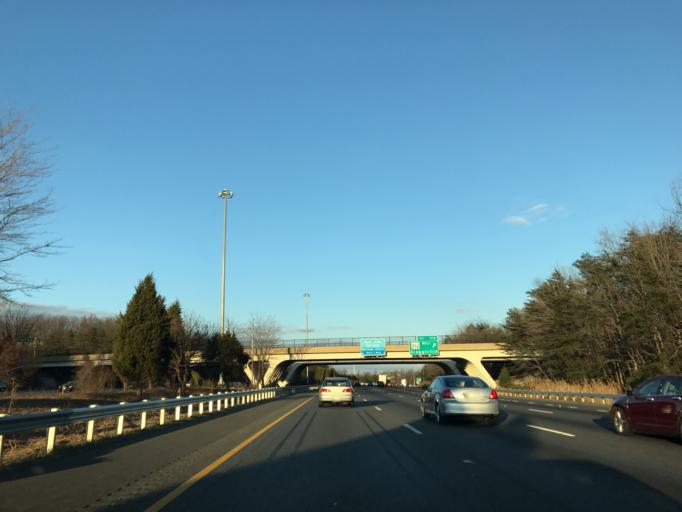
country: US
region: Maryland
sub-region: Howard County
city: North Laurel
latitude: 39.1282
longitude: -76.8631
